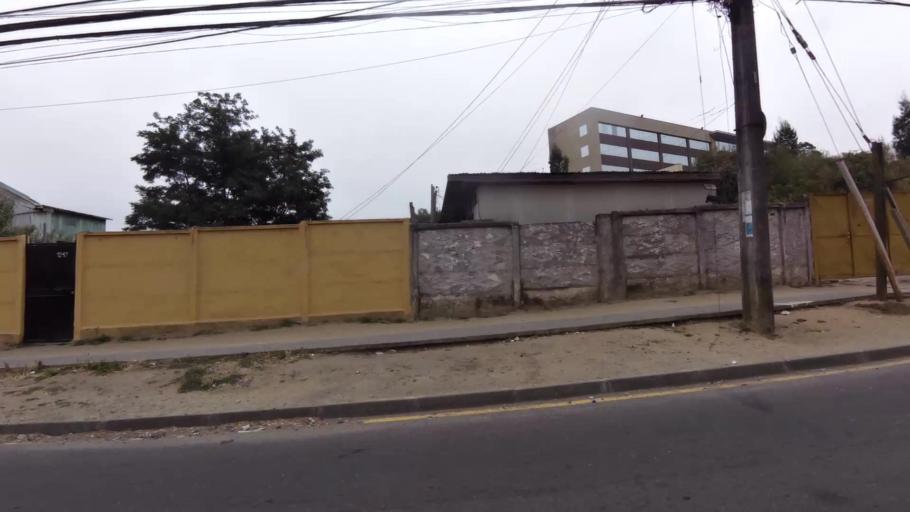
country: CL
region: Biobio
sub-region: Provincia de Concepcion
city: Concepcion
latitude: -36.8126
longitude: -73.0411
